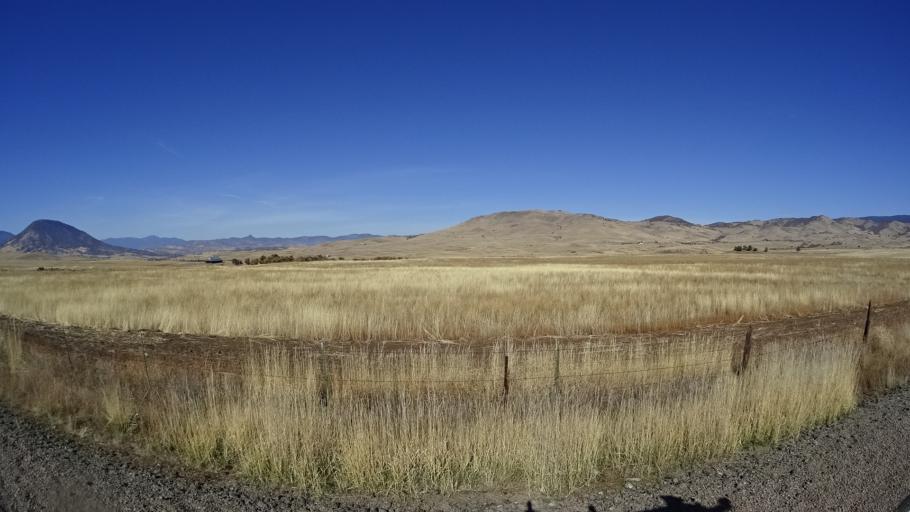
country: US
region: California
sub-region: Siskiyou County
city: Montague
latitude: 41.8044
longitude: -122.4101
